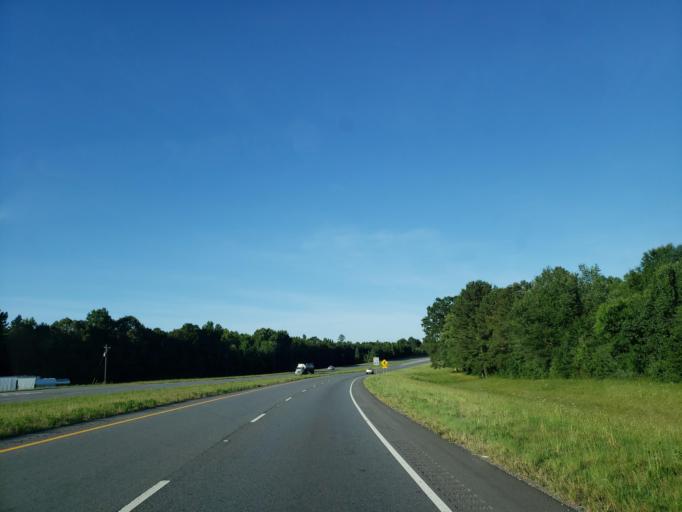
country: US
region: Georgia
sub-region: Floyd County
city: Shannon
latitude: 34.3302
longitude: -85.0968
